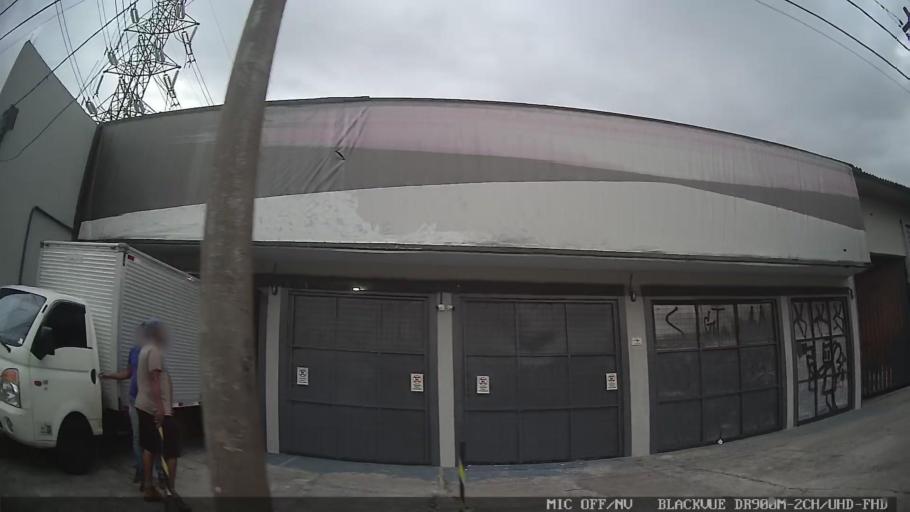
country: BR
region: Sao Paulo
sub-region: Mogi das Cruzes
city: Mogi das Cruzes
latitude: -23.5296
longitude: -46.1936
